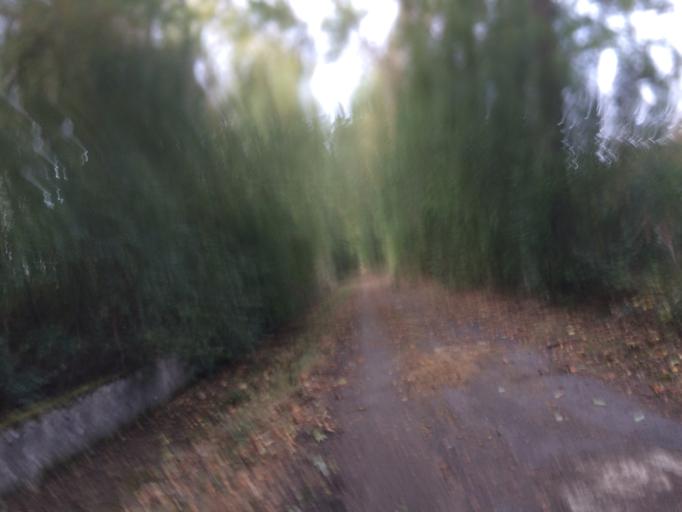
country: FR
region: Ile-de-France
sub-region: Departement de l'Essonne
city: Limours
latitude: 48.6586
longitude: 2.0892
